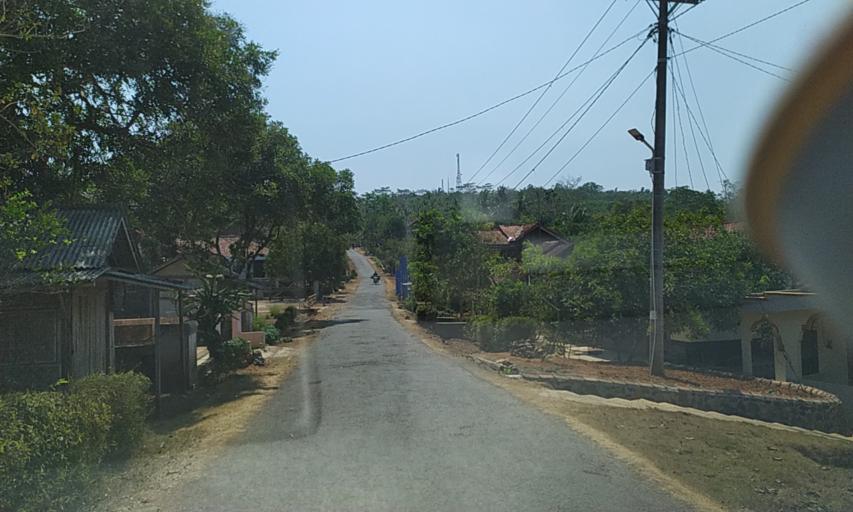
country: ID
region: Central Java
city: Rungkang
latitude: -7.4343
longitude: 108.8506
